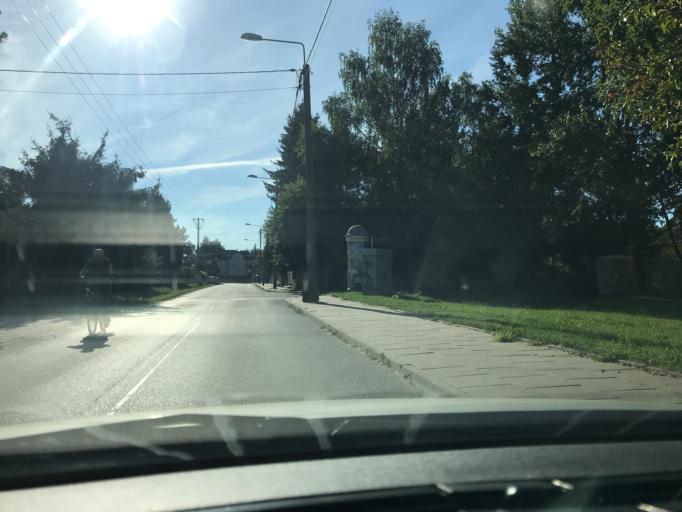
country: PL
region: Masovian Voivodeship
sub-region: Powiat pruszkowski
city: Piastow
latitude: 52.1686
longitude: 20.8383
